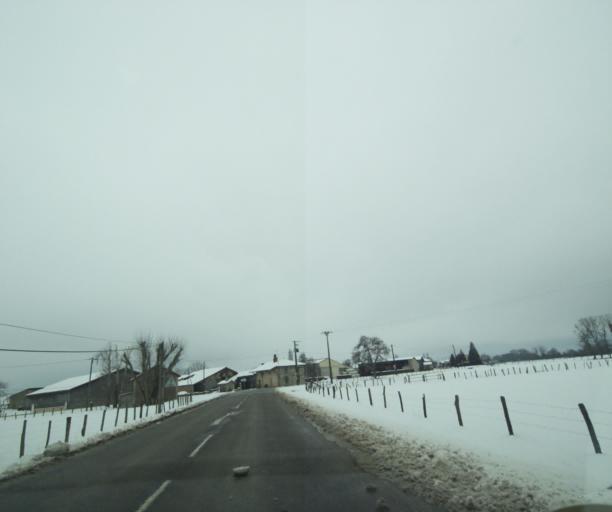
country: FR
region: Champagne-Ardenne
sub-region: Departement de la Haute-Marne
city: Montier-en-Der
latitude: 48.4564
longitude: 4.7703
